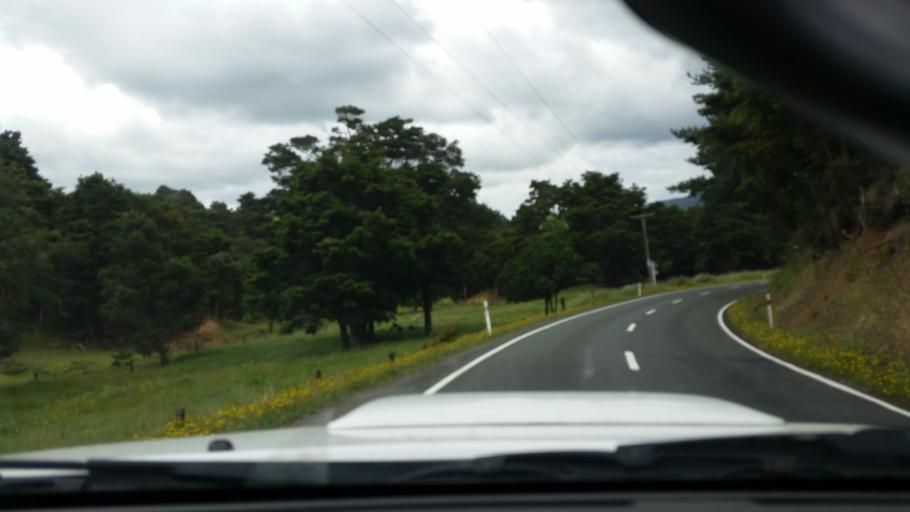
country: NZ
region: Northland
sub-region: Kaipara District
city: Dargaville
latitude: -35.8113
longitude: 173.7273
